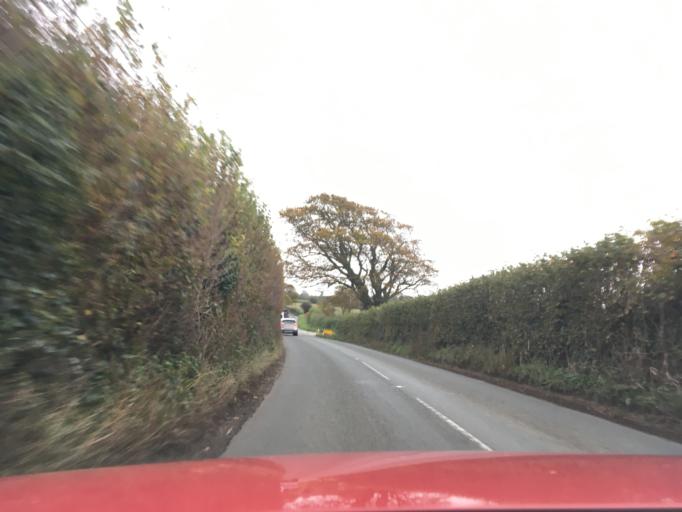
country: GB
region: England
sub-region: Dorset
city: Sherborne
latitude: 50.9798
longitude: -2.5641
